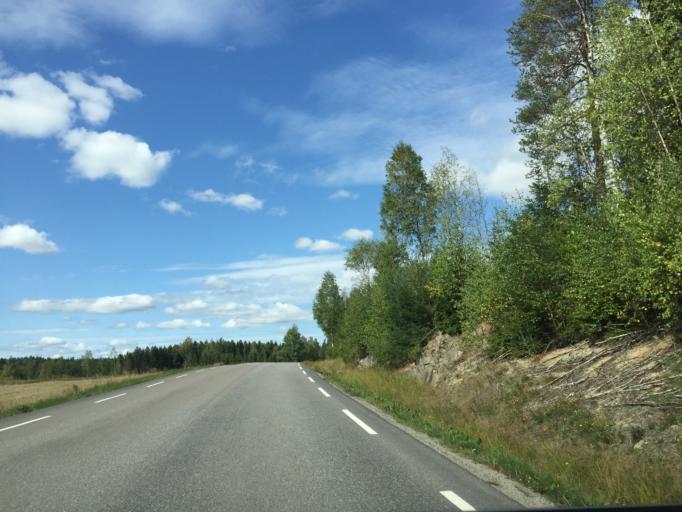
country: NO
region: Ostfold
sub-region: Hobol
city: Elvestad
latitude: 59.6048
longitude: 10.9052
